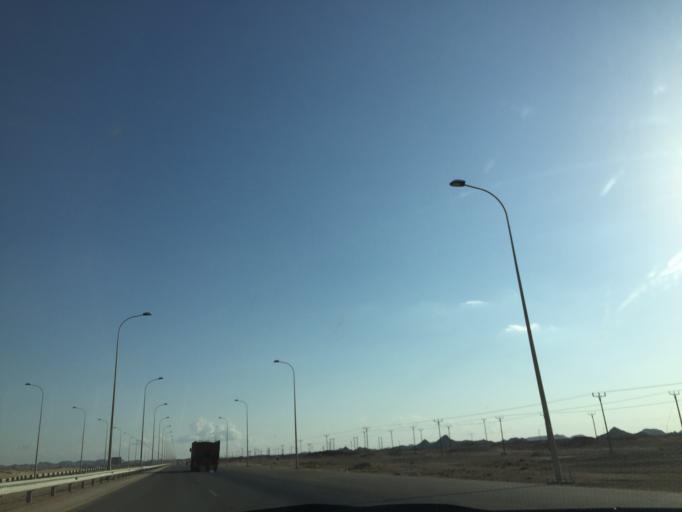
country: OM
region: Zufar
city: Salalah
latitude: 17.5306
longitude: 54.0556
